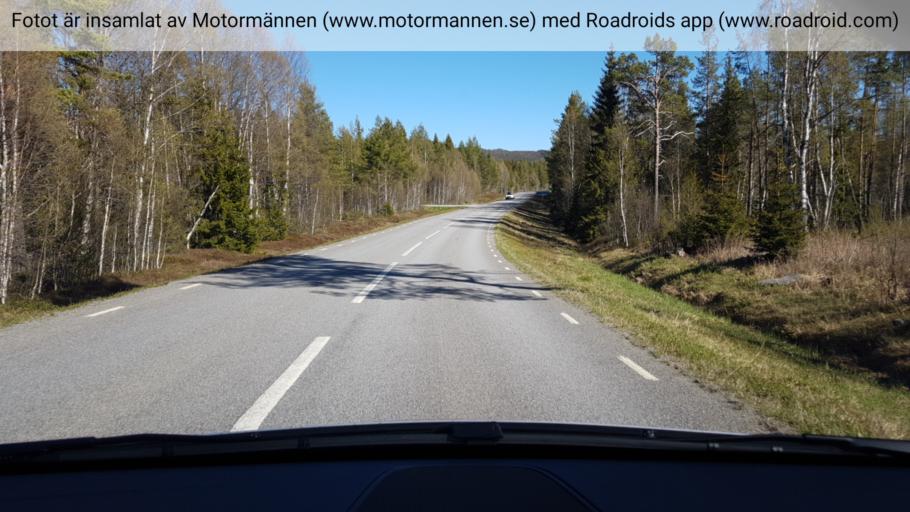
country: NO
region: Nord-Trondelag
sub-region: Lierne
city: Sandvika
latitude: 64.3992
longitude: 14.5008
